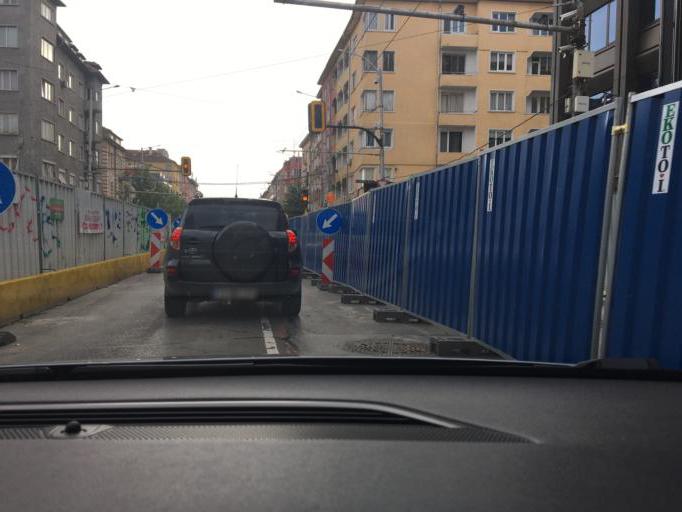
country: BG
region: Sofia-Capital
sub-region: Stolichna Obshtina
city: Sofia
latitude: 42.6879
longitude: 23.3287
